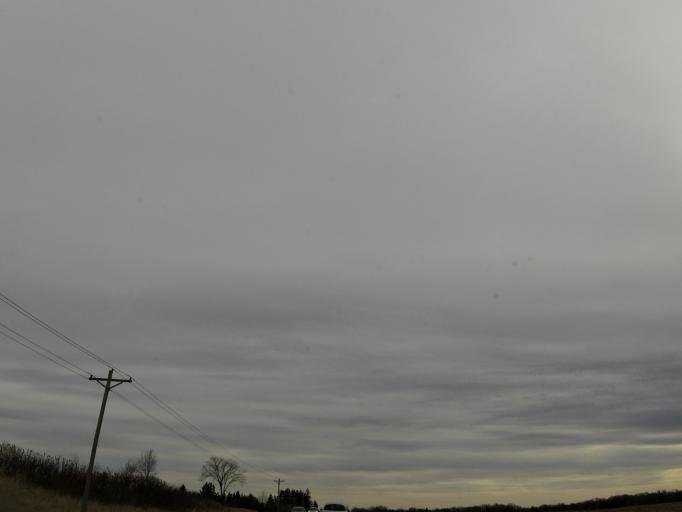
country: US
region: Minnesota
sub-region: Scott County
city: Prior Lake
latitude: 44.7096
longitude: -93.3793
